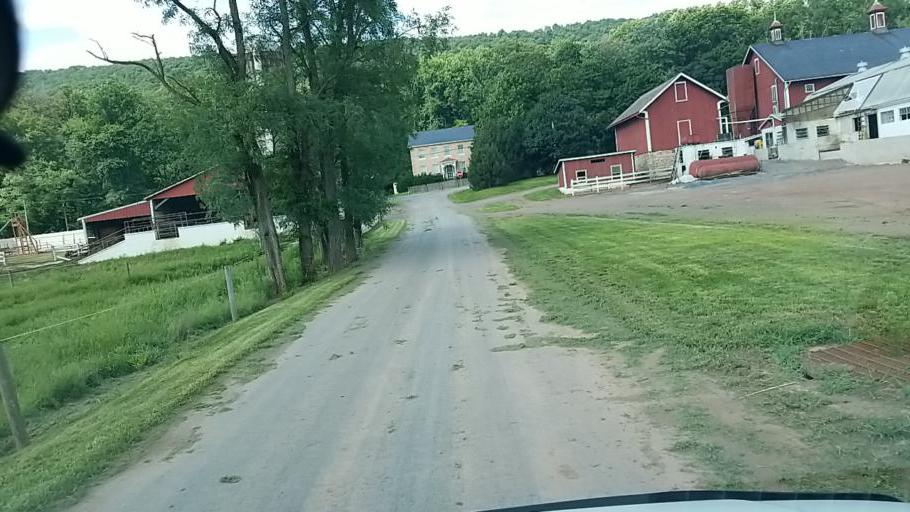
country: US
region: Pennsylvania
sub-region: Dauphin County
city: Elizabethville
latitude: 40.6094
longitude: -76.8536
